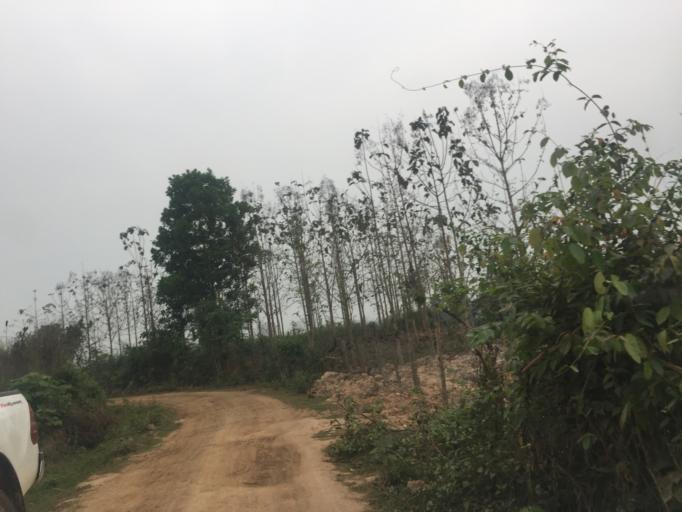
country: LA
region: Xiagnabouli
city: Sainyabuli
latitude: 19.0025
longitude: 101.5159
